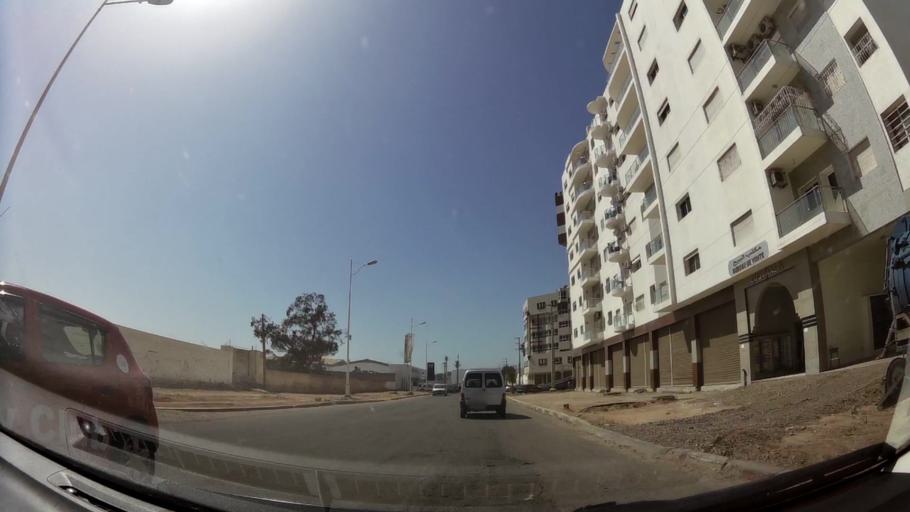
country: MA
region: Souss-Massa-Draa
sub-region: Agadir-Ida-ou-Tnan
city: Agadir
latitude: 30.4187
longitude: -9.5775
